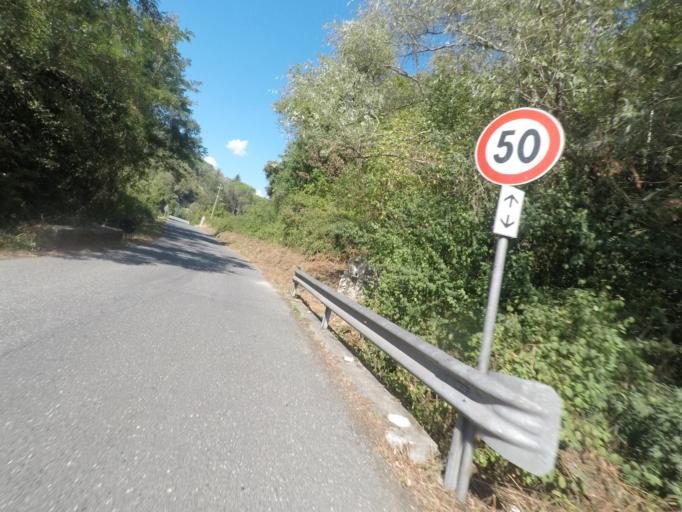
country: IT
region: Tuscany
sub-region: Provincia di Massa-Carrara
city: Pallerone
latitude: 44.2002
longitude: 10.0612
